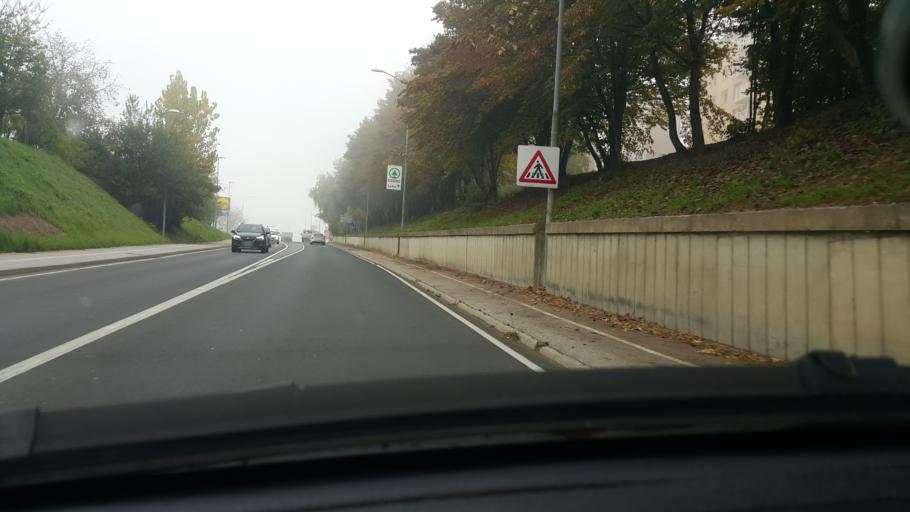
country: SI
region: Brezice
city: Brezice
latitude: 45.9034
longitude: 15.6037
